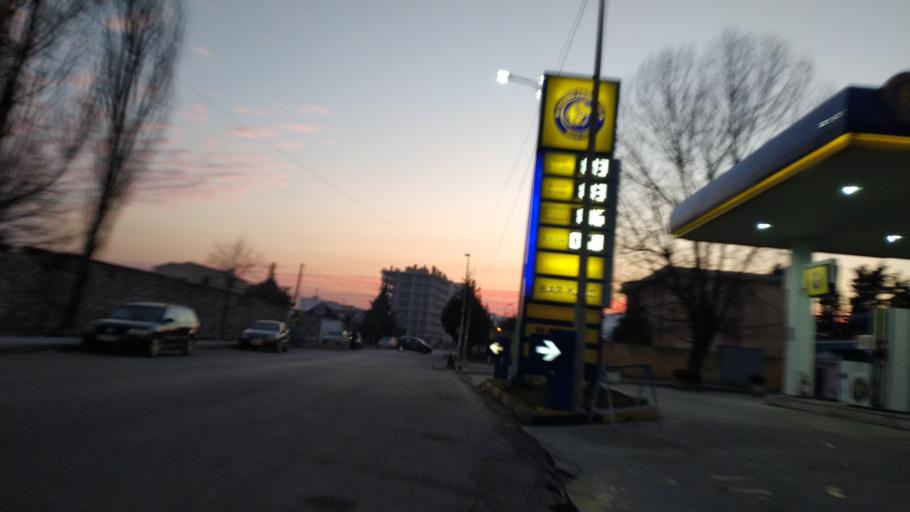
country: AL
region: Shkoder
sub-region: Rrethi i Shkodres
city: Shkoder
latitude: 42.0798
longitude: 19.5236
